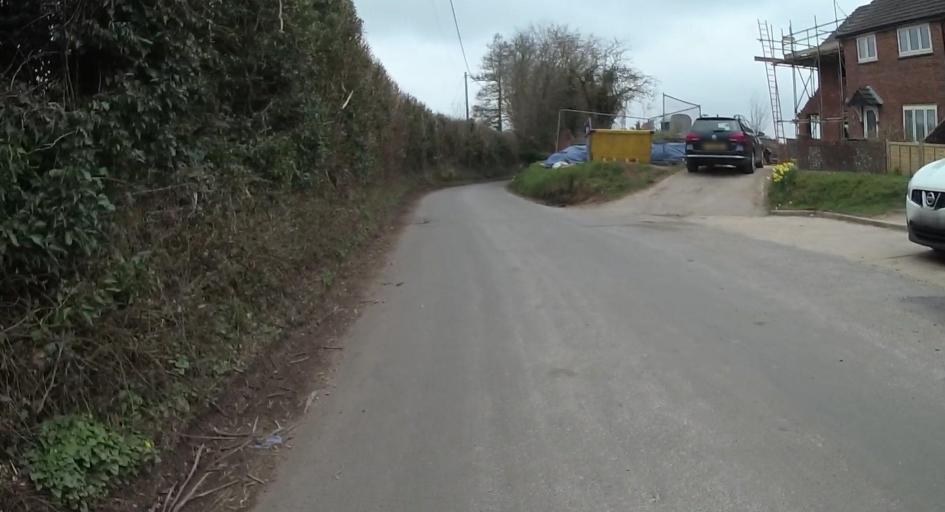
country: GB
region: England
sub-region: Hampshire
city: Four Marks
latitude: 51.0845
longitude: -1.0789
